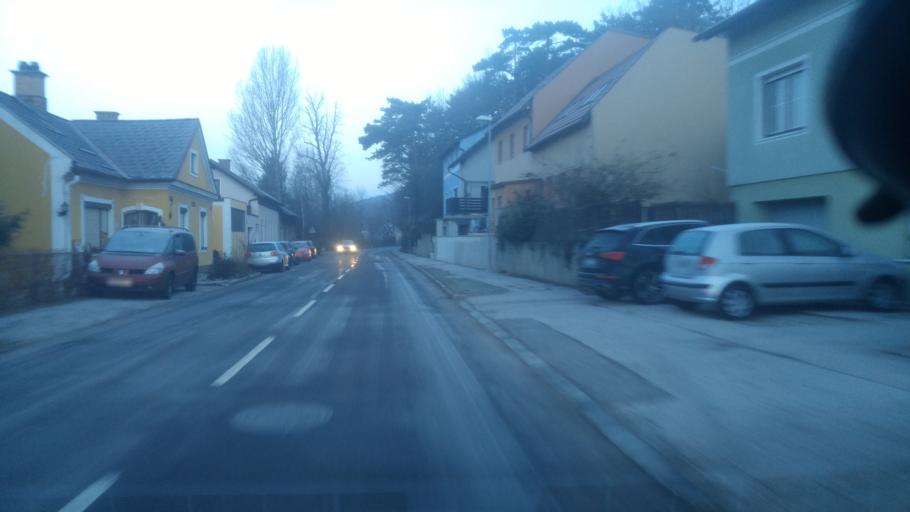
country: AT
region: Lower Austria
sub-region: Politischer Bezirk Baden
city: Berndorf
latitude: 47.9532
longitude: 16.1048
